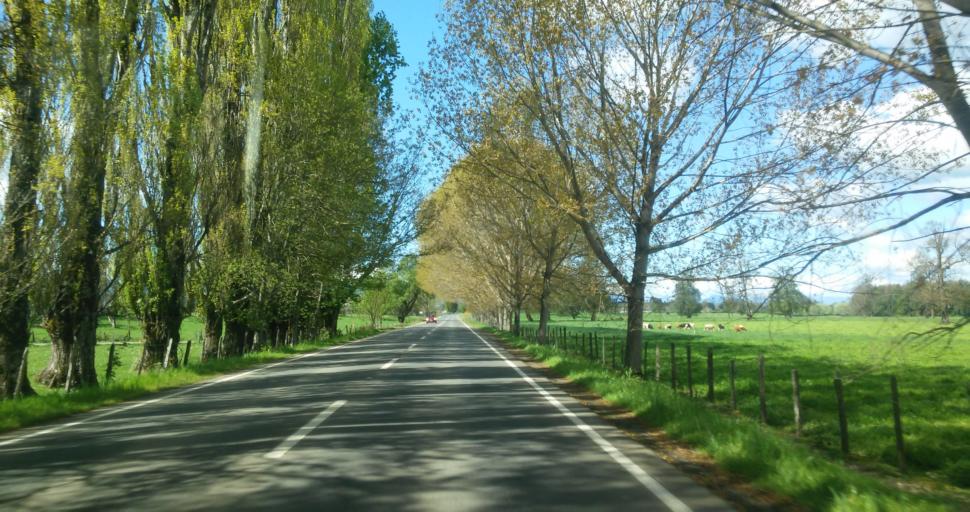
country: CL
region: Los Rios
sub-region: Provincia del Ranco
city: Rio Bueno
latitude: -40.2422
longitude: -72.6104
